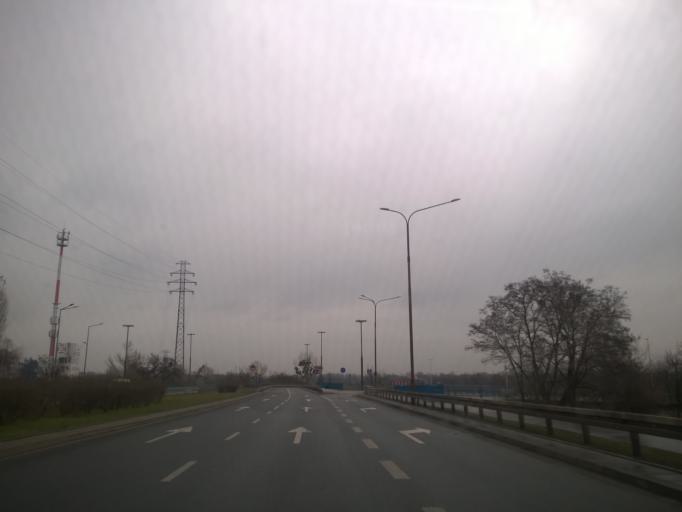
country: PL
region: Lower Silesian Voivodeship
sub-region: Powiat wroclawski
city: Wroclaw
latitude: 51.0864
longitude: 17.0676
